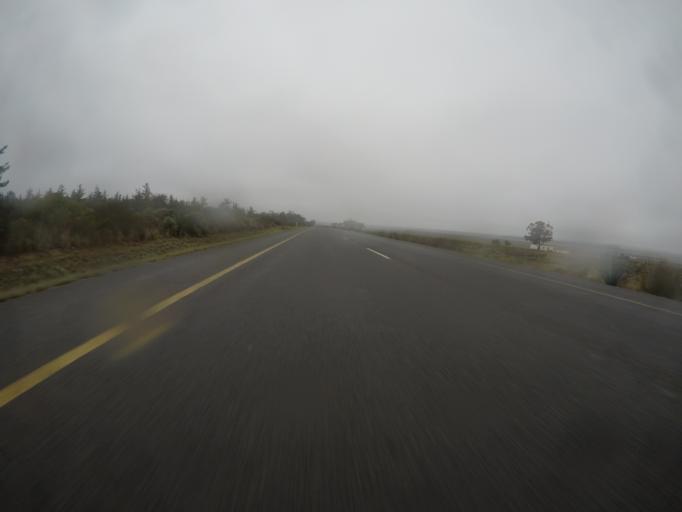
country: ZA
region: Western Cape
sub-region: Eden District Municipality
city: Riversdale
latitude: -34.1935
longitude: 21.4733
